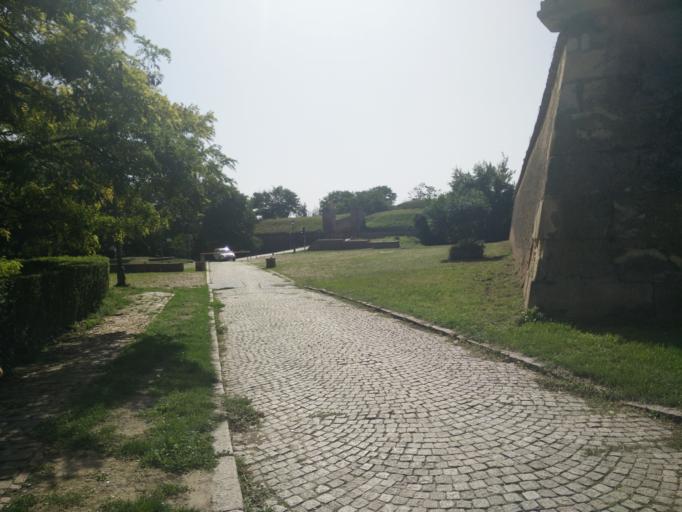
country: RS
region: Autonomna Pokrajina Vojvodina
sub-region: Juznobacki Okrug
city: Petrovaradin
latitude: 45.2517
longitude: 19.8646
